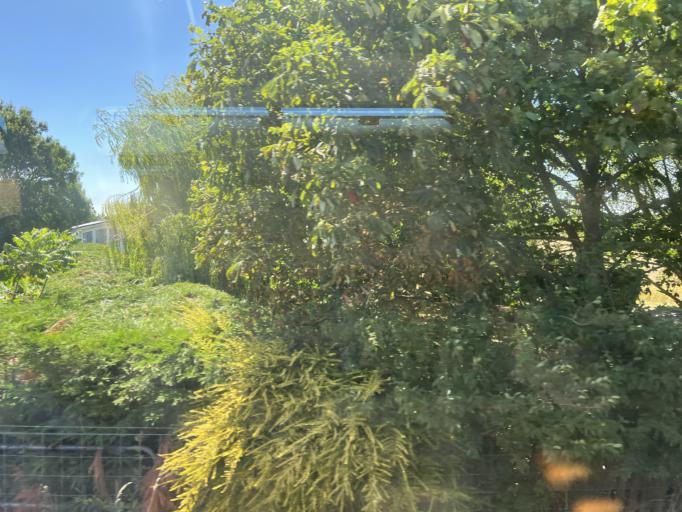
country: GB
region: England
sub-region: Lincolnshire
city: Wainfleet All Saints
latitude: 53.1120
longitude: 0.2198
